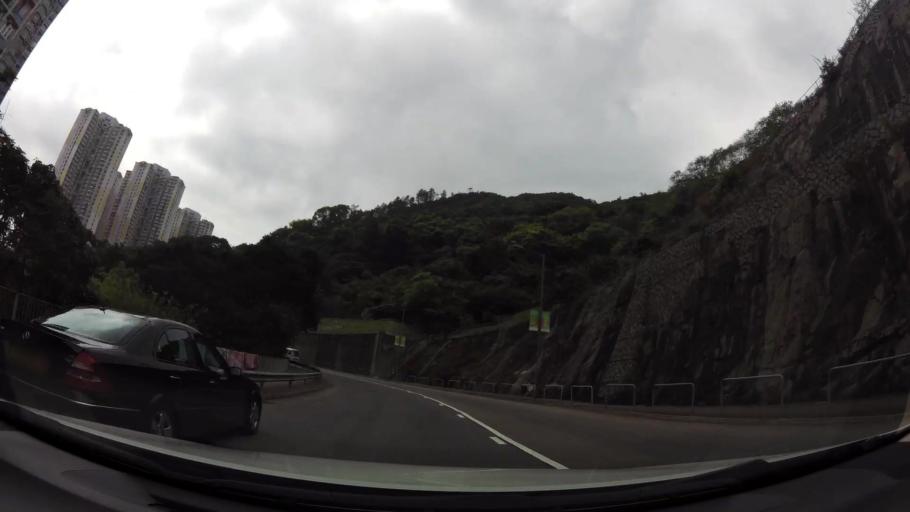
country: HK
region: Wanchai
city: Wan Chai
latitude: 22.2794
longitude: 114.2185
